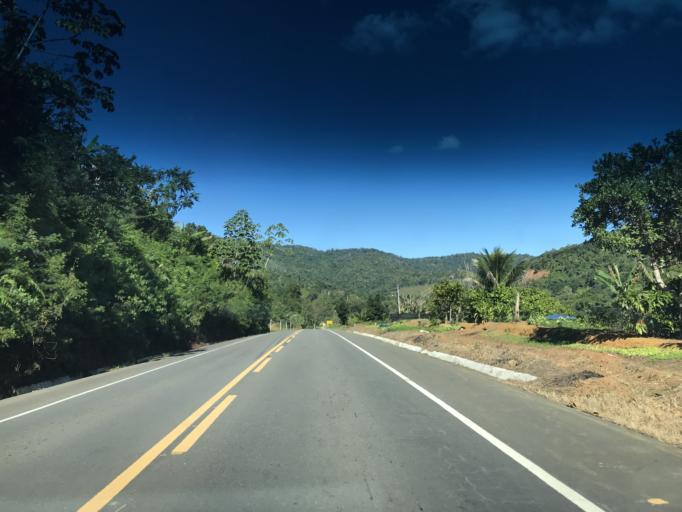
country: BR
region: Bahia
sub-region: Gandu
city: Gandu
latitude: -13.8862
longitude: -39.4828
